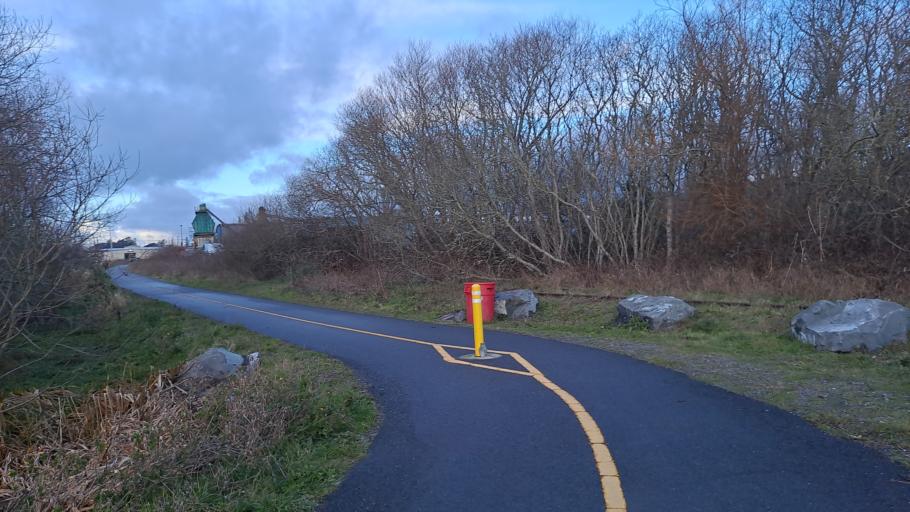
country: US
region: California
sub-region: Humboldt County
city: Arcata
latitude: 40.8636
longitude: -124.0932
